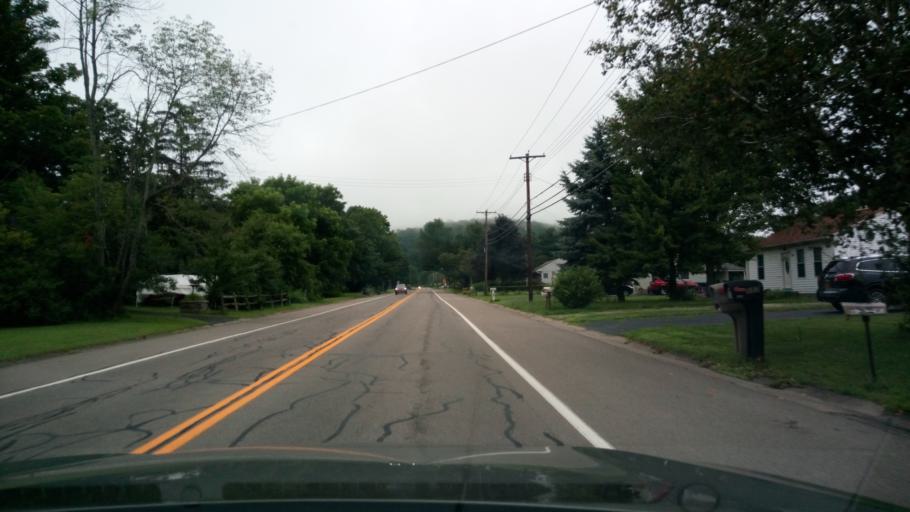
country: US
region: New York
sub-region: Chemung County
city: West Elmira
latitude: 42.0816
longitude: -76.8764
